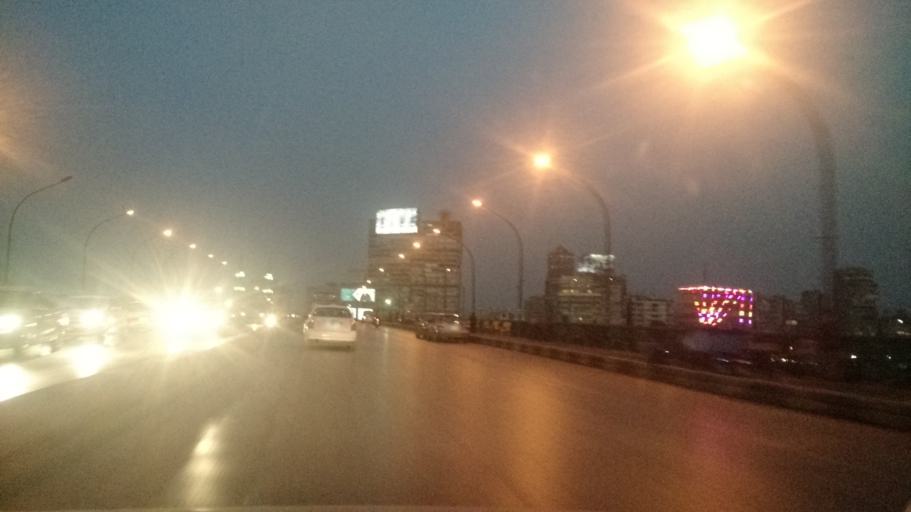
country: EG
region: Al Jizah
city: Al Jizah
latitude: 30.0285
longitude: 31.2192
